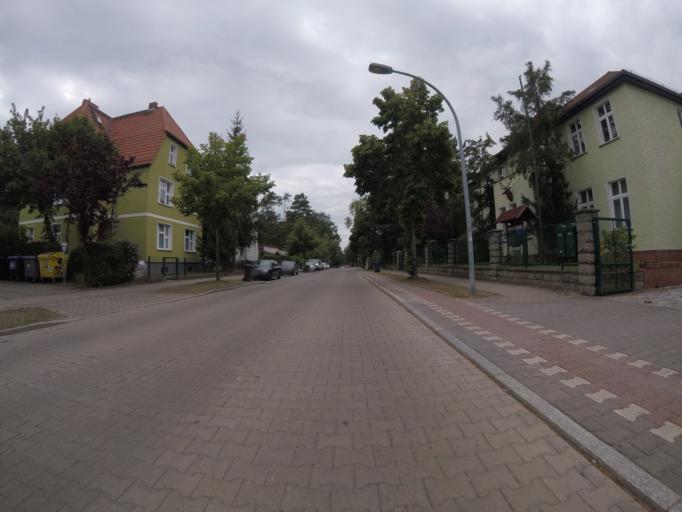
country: DE
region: Brandenburg
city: Birkenwerder
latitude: 52.7148
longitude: 13.2737
